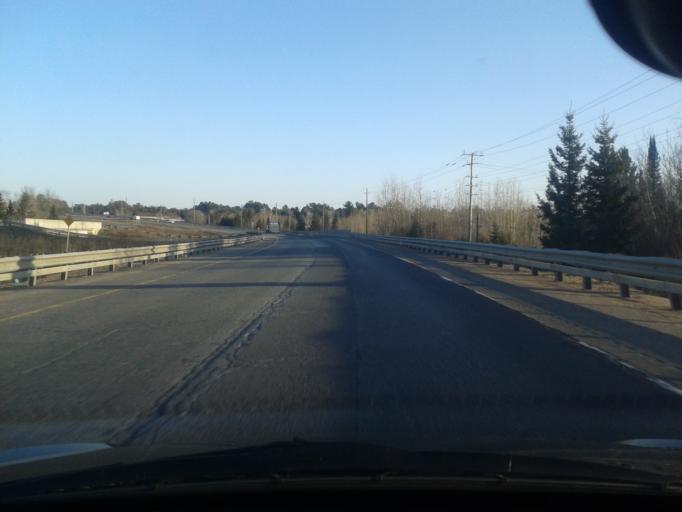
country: CA
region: Ontario
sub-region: Nipissing District
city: North Bay
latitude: 46.2727
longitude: -79.4015
